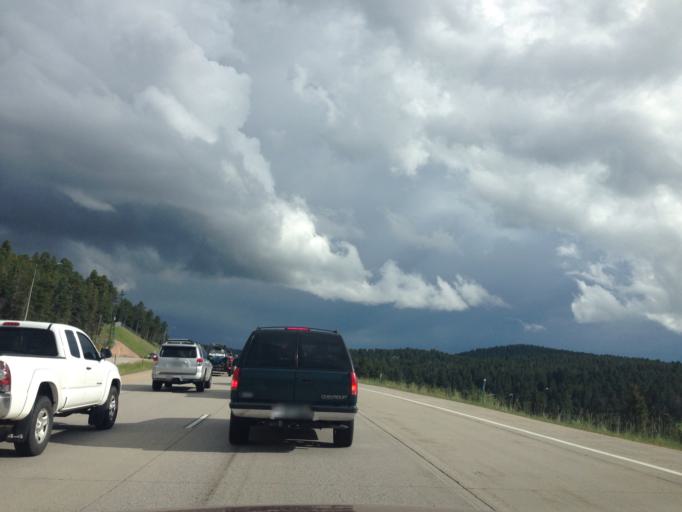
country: US
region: Colorado
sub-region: Jefferson County
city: Evergreen
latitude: 39.5274
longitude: -105.3076
